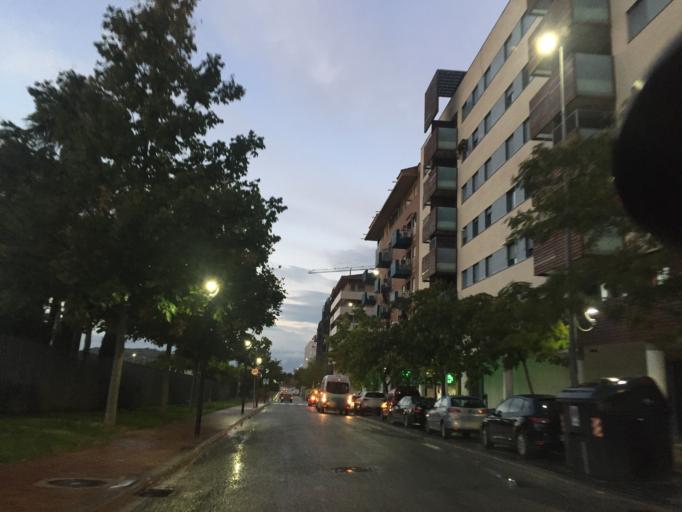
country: ES
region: Andalusia
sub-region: Provincia de Jaen
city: Jaen
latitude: 37.7871
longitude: -3.7901
